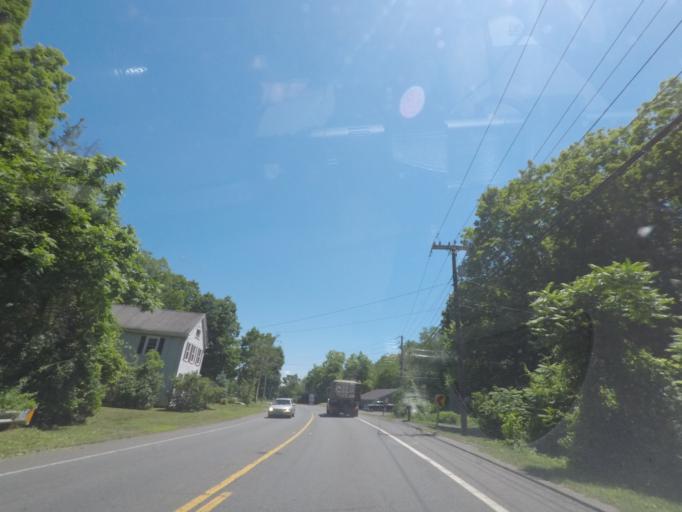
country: US
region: Massachusetts
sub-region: Hampden County
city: Westfield
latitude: 42.1488
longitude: -72.8141
